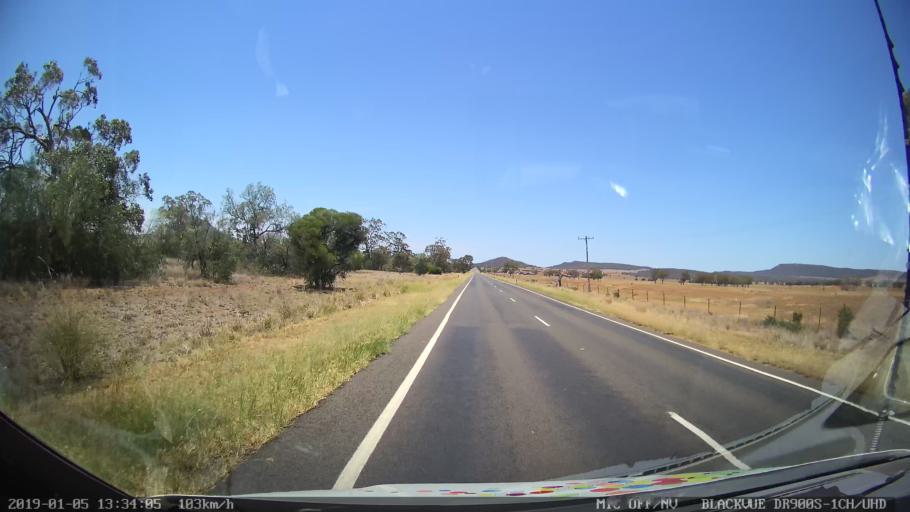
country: AU
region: New South Wales
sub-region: Gunnedah
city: Gunnedah
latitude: -30.9974
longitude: 150.1273
